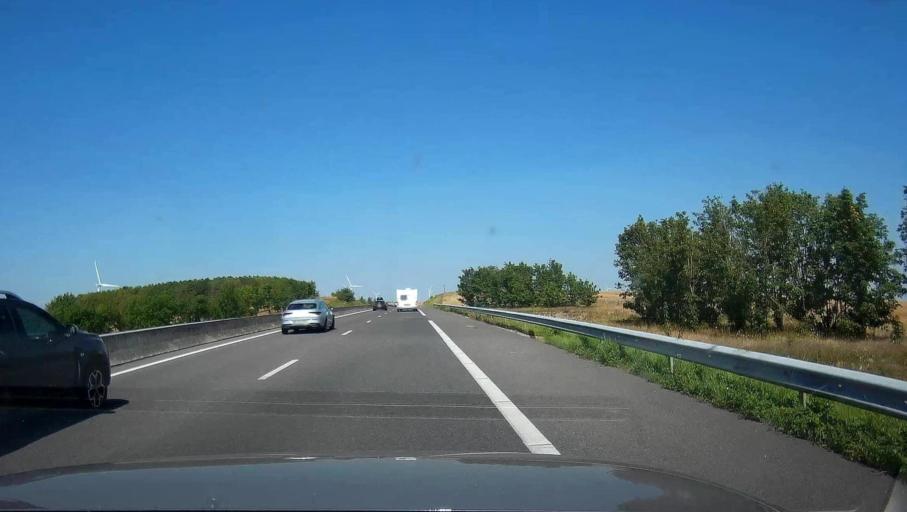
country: FR
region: Champagne-Ardenne
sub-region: Departement de l'Aube
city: Arcis-sur-Aube
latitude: 48.5848
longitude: 4.1852
